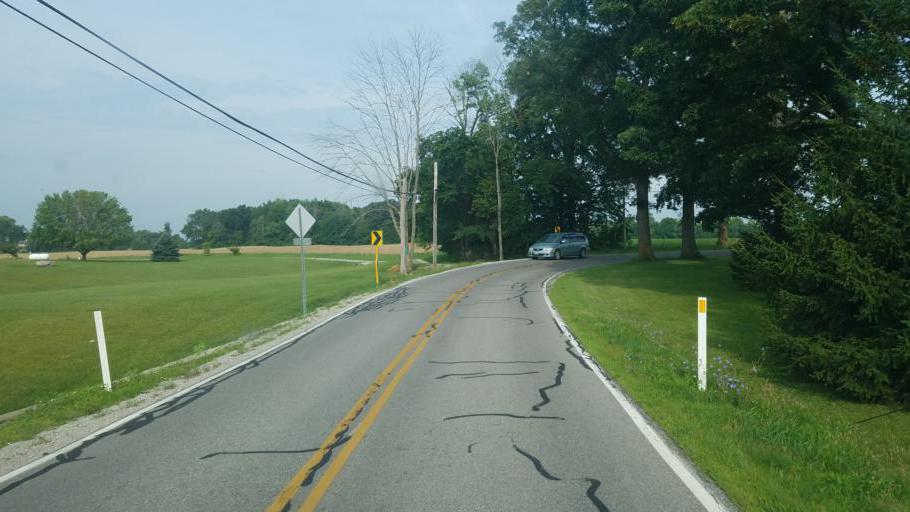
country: US
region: Ohio
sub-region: Marion County
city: Marion
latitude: 40.5128
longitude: -83.0622
